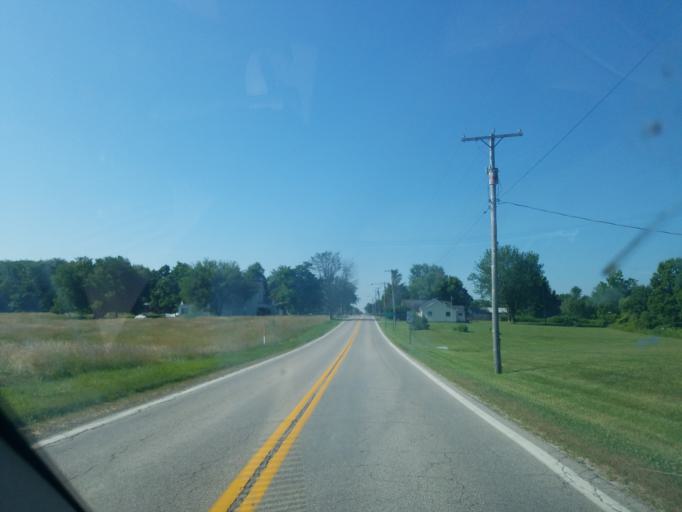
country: US
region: Ohio
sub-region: Union County
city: Richwood
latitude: 40.4103
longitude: -83.4531
